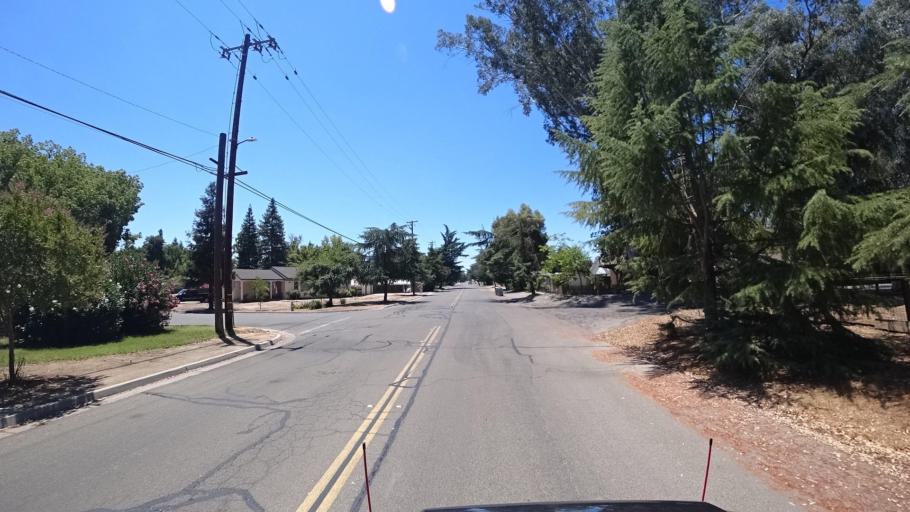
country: US
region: California
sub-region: Fresno County
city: Fresno
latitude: 36.7897
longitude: -119.8024
